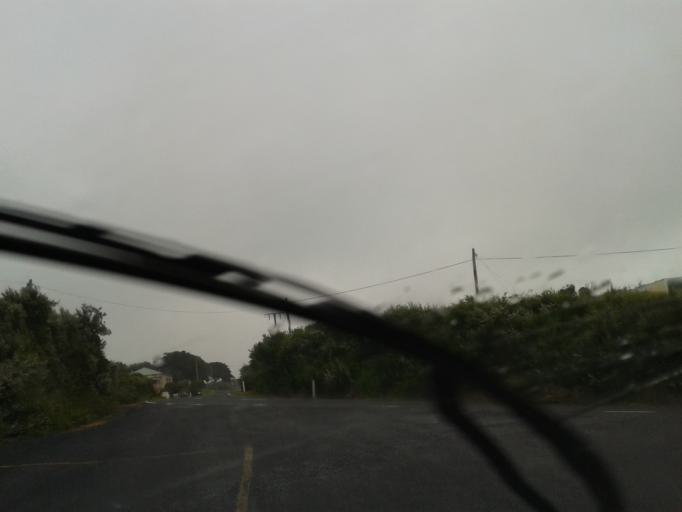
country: AU
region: Victoria
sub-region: Glenelg
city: Portland
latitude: -38.3707
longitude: 141.4047
